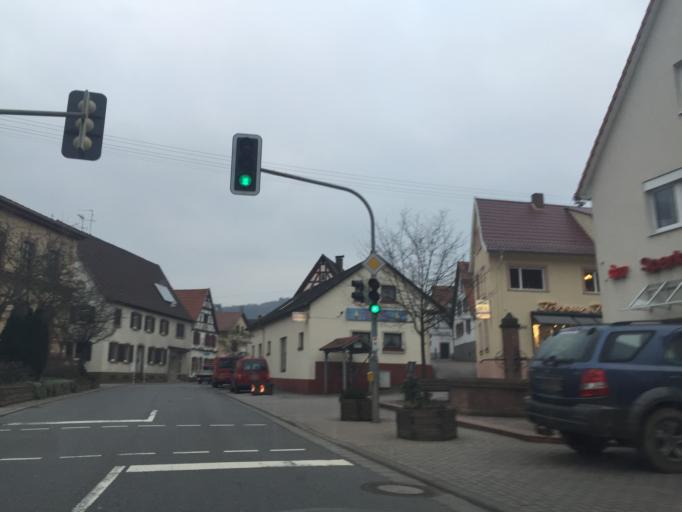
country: DE
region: Baden-Wuerttemberg
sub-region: Karlsruhe Region
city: Weinheim
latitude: 49.5116
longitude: 8.6600
